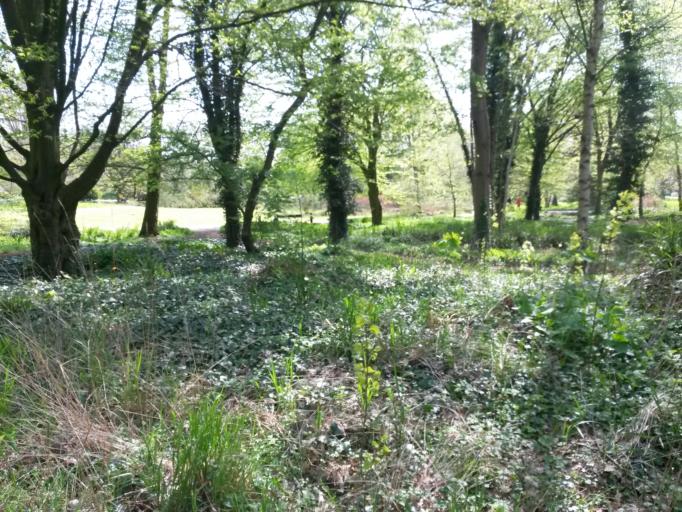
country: DE
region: Hamburg
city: Eidelstedt
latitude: 53.5633
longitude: 9.8585
